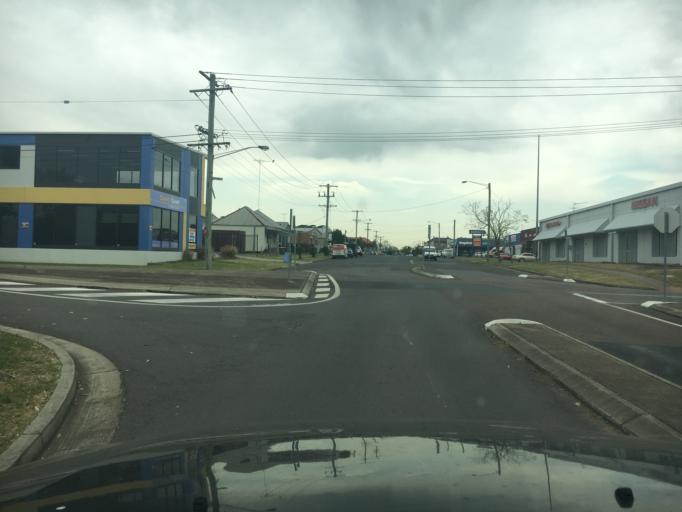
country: AU
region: New South Wales
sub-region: Maitland Municipality
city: East Maitland
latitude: -32.7485
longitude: 151.5786
